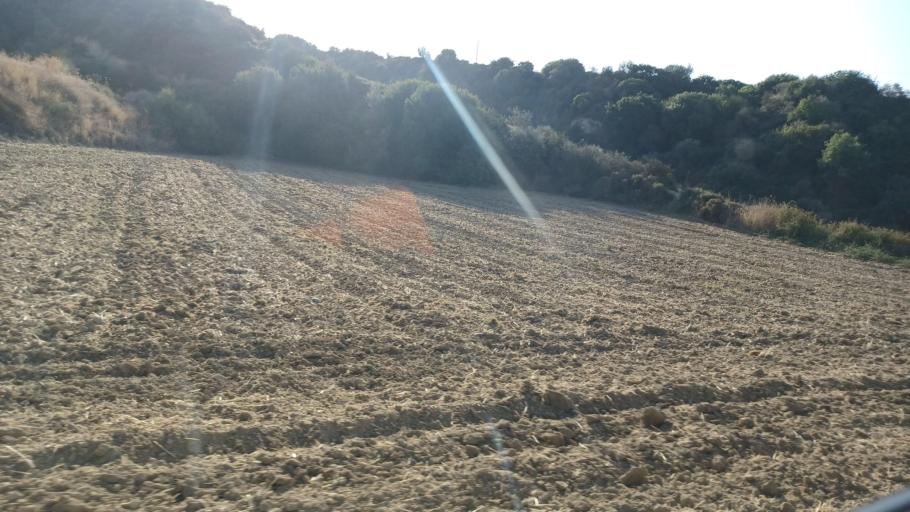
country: CY
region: Pafos
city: Polis
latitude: 35.0009
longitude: 32.4565
